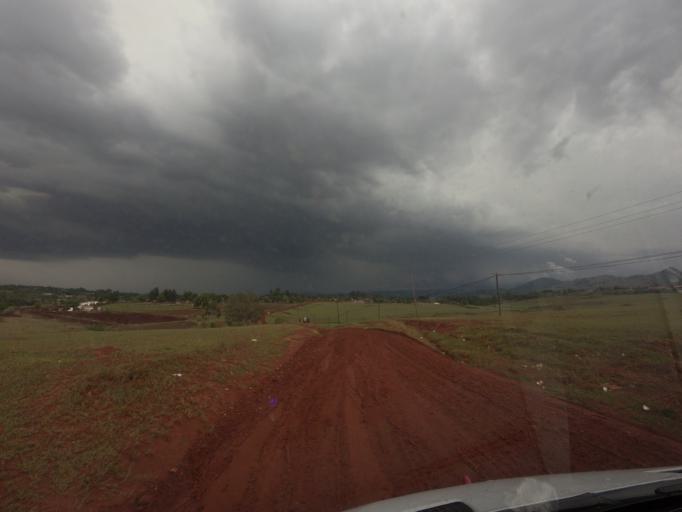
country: SZ
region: Hhohho
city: Lobamba
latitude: -26.4618
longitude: 31.2173
